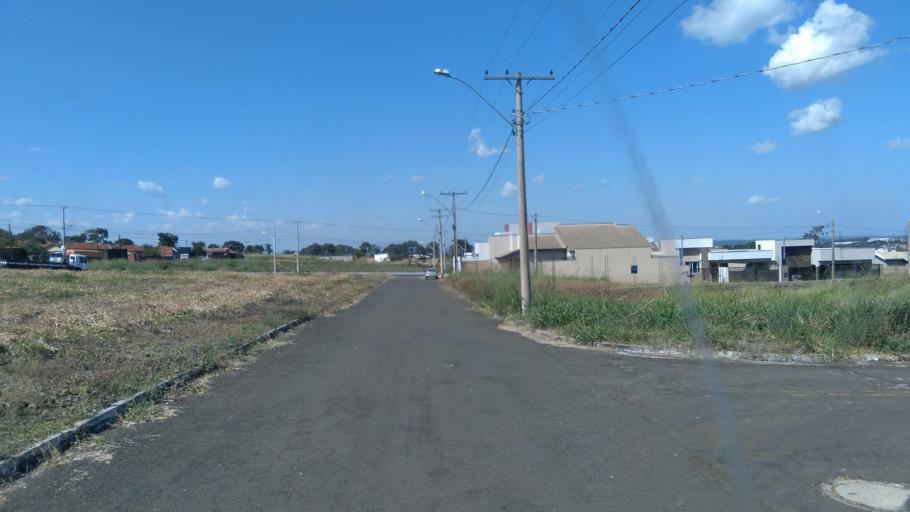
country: BR
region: Goias
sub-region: Mineiros
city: Mineiros
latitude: -17.5503
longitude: -52.5424
